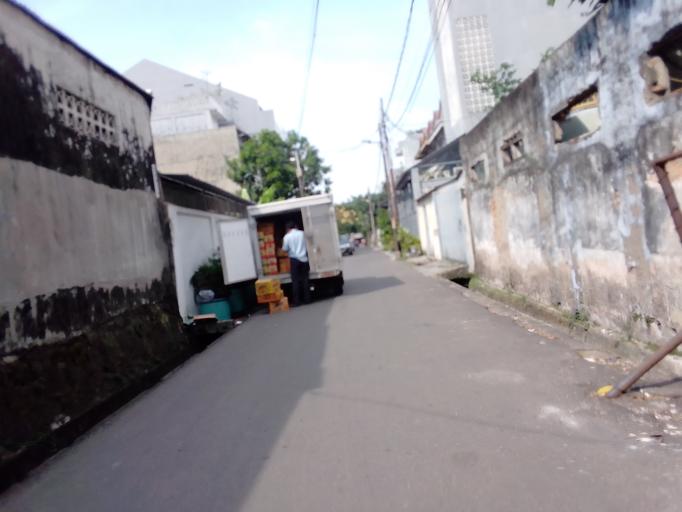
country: ID
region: Jakarta Raya
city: Jakarta
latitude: -6.1624
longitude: 106.8108
